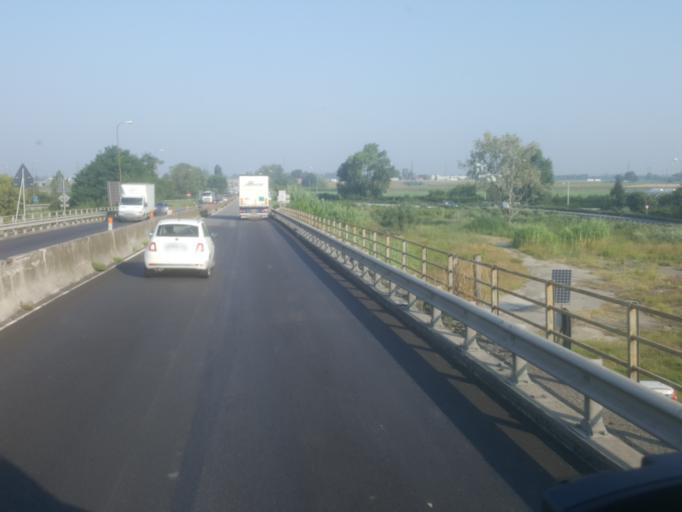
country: IT
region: Emilia-Romagna
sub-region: Provincia di Ravenna
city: Fornace Zarattini
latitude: 44.4224
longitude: 12.1623
